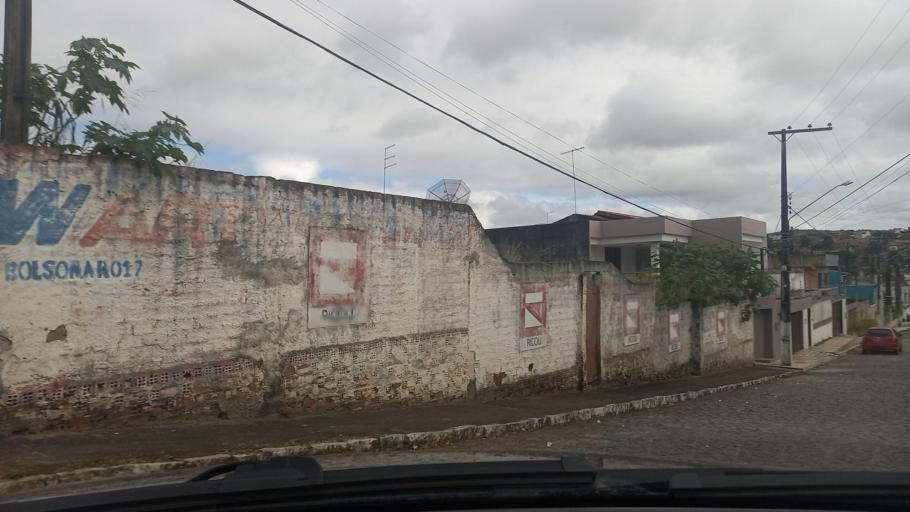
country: BR
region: Pernambuco
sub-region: Vitoria De Santo Antao
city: Vitoria de Santo Antao
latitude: -8.1203
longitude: -35.3049
